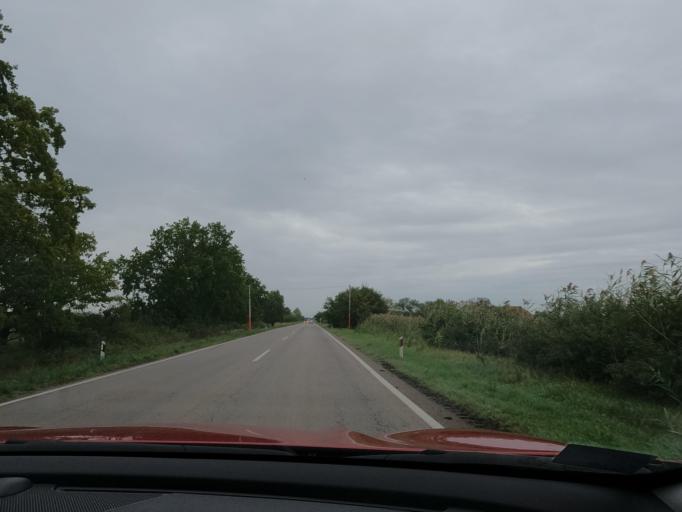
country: RS
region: Autonomna Pokrajina Vojvodina
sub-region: Severnobanatski Okrug
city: Kikinda
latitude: 45.7812
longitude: 20.4300
